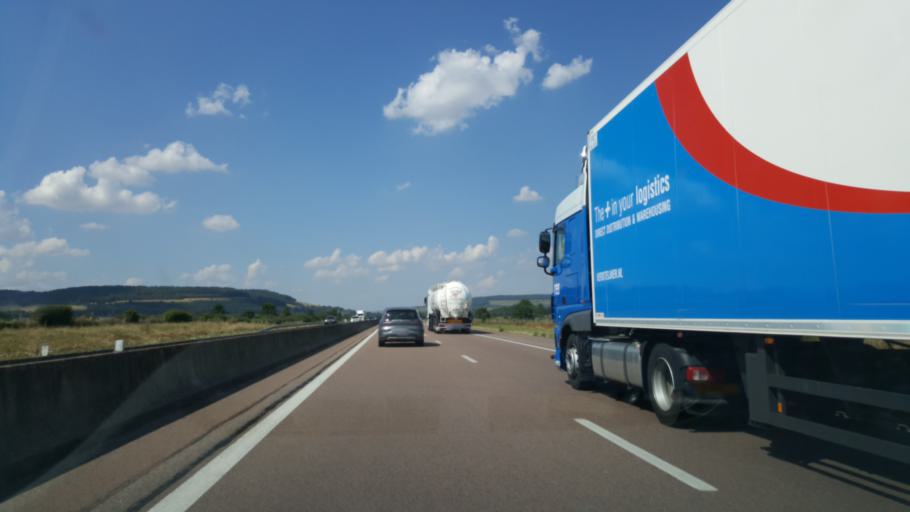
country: FR
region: Bourgogne
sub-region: Departement de la Cote-d'Or
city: Pouilly-en-Auxois
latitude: 47.2772
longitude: 4.5107
